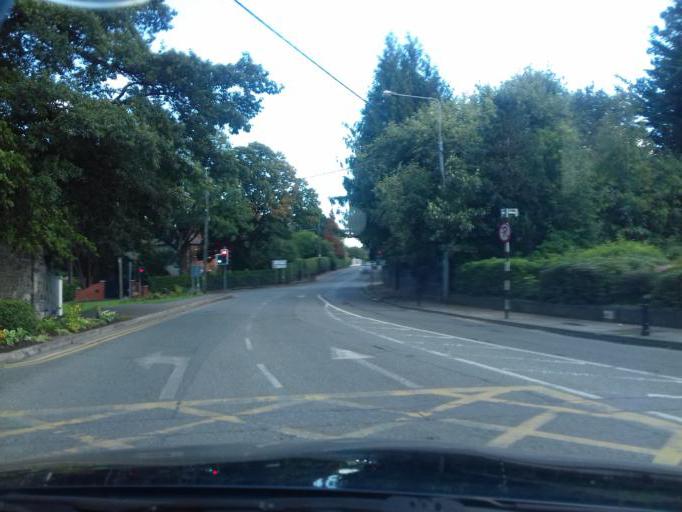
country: IE
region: Leinster
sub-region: Uibh Fhaili
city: Tullamore
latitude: 53.2704
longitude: -7.4912
